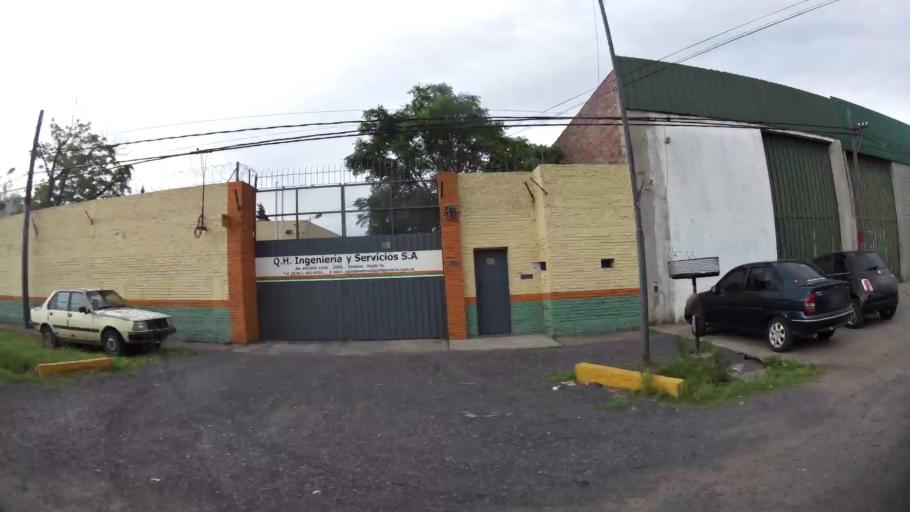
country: AR
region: Santa Fe
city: Gobernador Galvez
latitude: -33.0040
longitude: -60.6800
